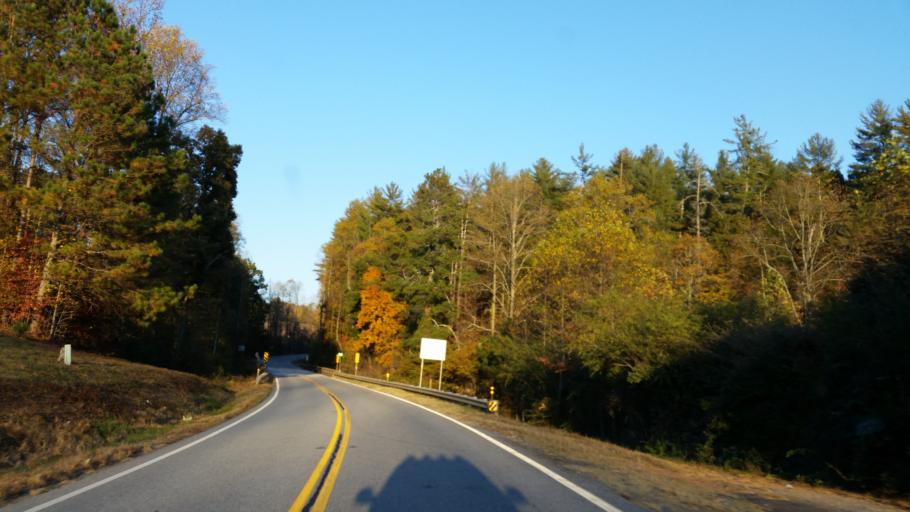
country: US
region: Georgia
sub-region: Lumpkin County
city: Dahlonega
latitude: 34.5344
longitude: -84.0643
